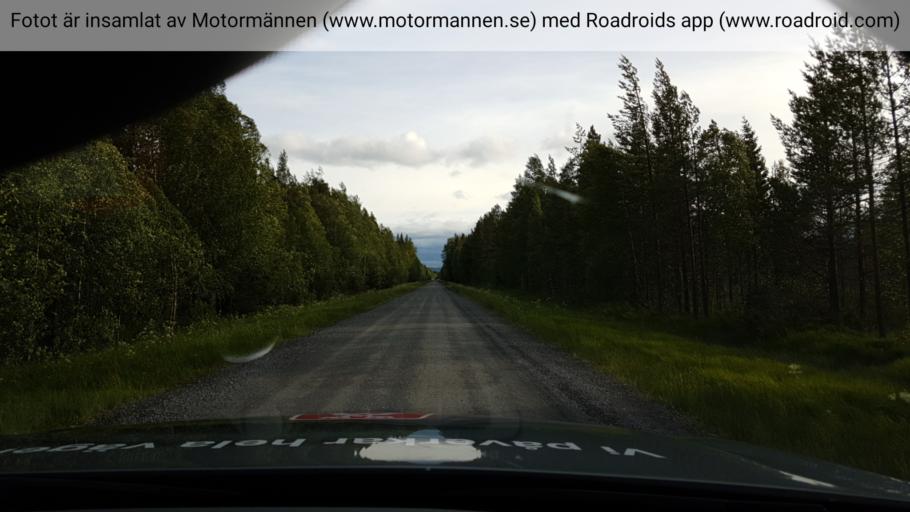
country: SE
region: Jaemtland
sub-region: Stroemsunds Kommun
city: Stroemsund
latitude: 63.7123
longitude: 15.1860
